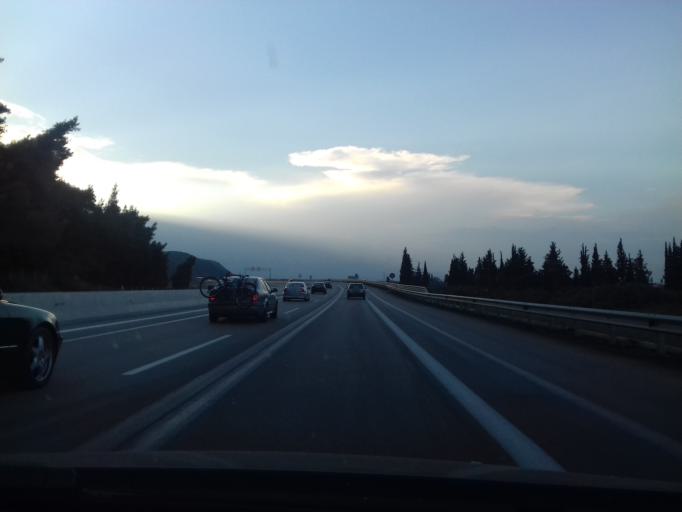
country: GR
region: West Greece
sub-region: Nomos Achaias
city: Temeni
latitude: 38.1883
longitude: 22.1752
